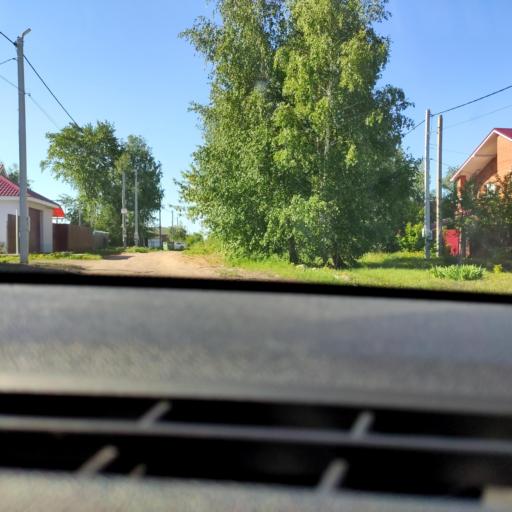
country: RU
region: Samara
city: Tol'yatti
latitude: 53.5591
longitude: 49.4097
